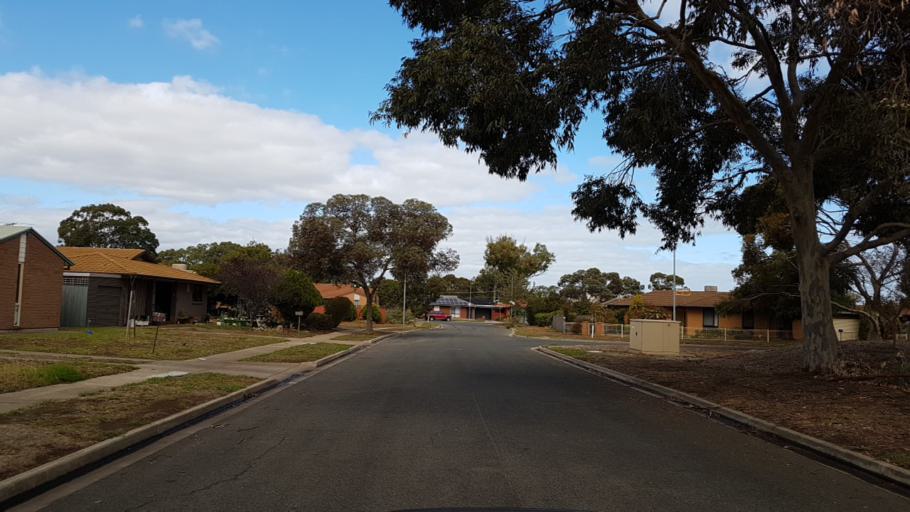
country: AU
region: South Australia
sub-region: Charles Sturt
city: Seaton
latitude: -34.9089
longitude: 138.5197
